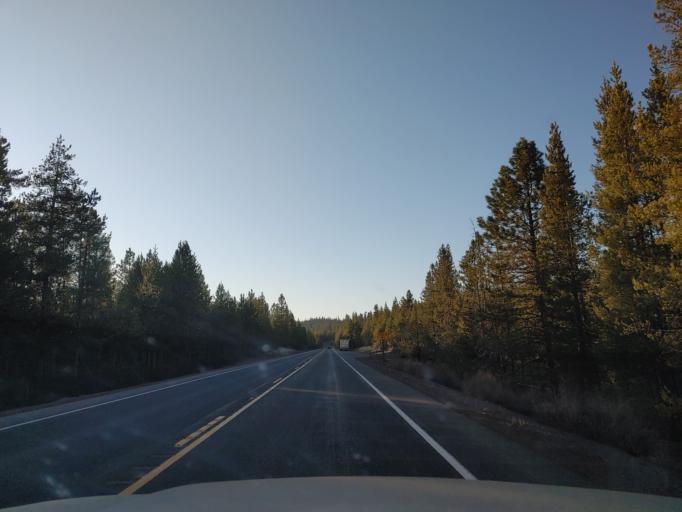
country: US
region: Oregon
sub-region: Deschutes County
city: La Pine
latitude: 43.4381
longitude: -121.8624
